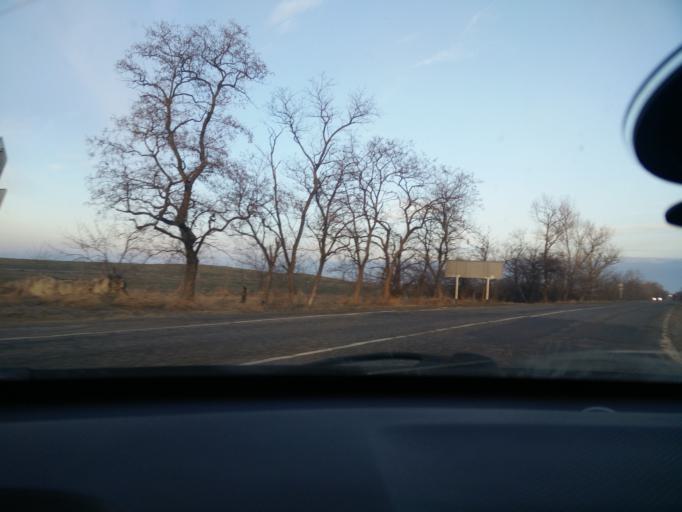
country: RU
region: Stavropol'skiy
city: Balakhonovskoye
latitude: 44.9777
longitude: 41.6866
